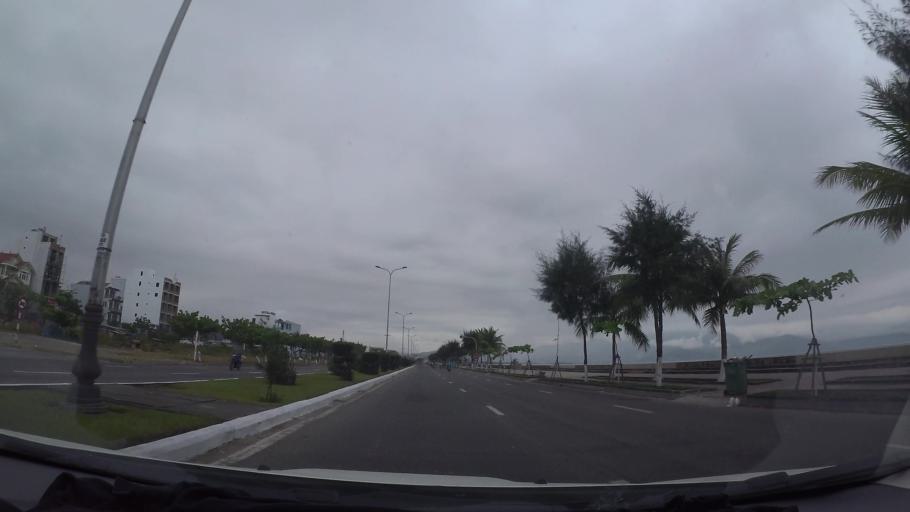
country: VN
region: Da Nang
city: Lien Chieu
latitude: 16.0822
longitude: 108.1649
